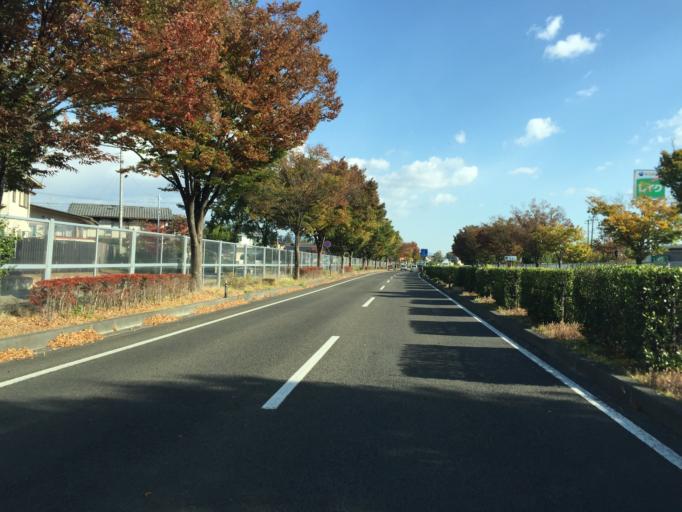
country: JP
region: Fukushima
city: Fukushima-shi
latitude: 37.7728
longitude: 140.4413
